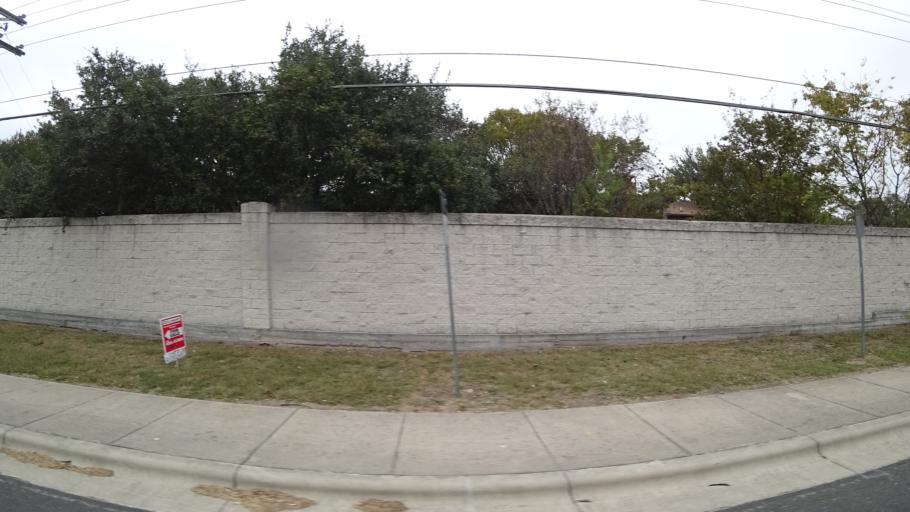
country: US
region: Texas
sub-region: Williamson County
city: Anderson Mill
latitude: 30.4503
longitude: -97.8181
